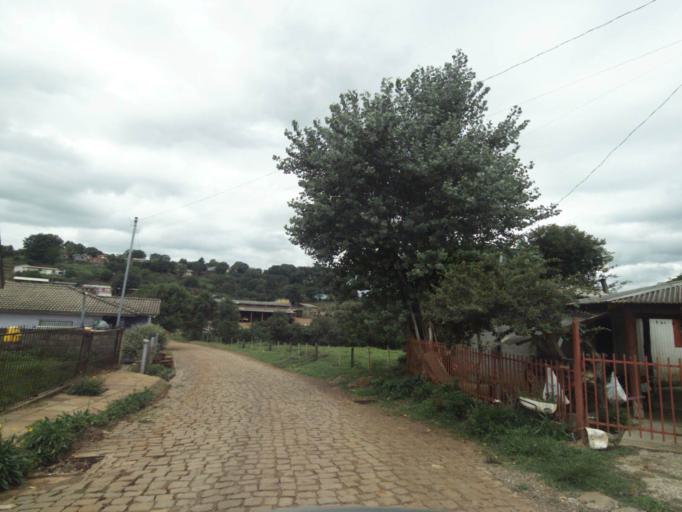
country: BR
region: Rio Grande do Sul
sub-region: Lagoa Vermelha
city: Lagoa Vermelha
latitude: -28.2133
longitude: -51.5419
